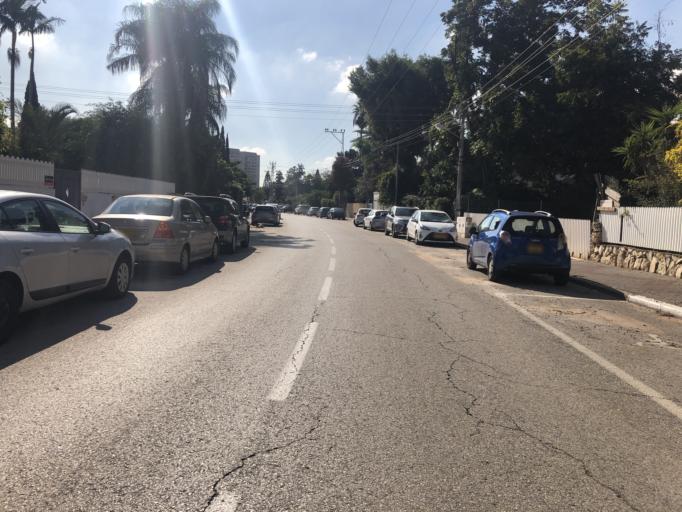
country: IL
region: Tel Aviv
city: Or Yehuda
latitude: 32.0316
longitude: 34.8697
